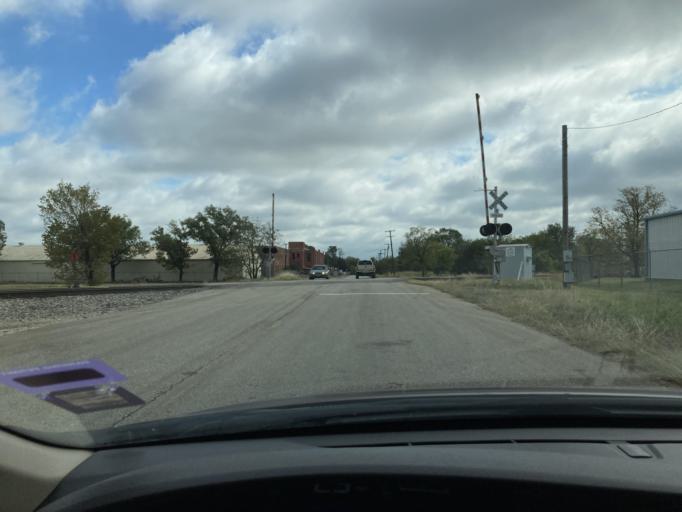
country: US
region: Texas
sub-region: Navarro County
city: Corsicana
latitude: 32.0893
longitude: -96.4623
